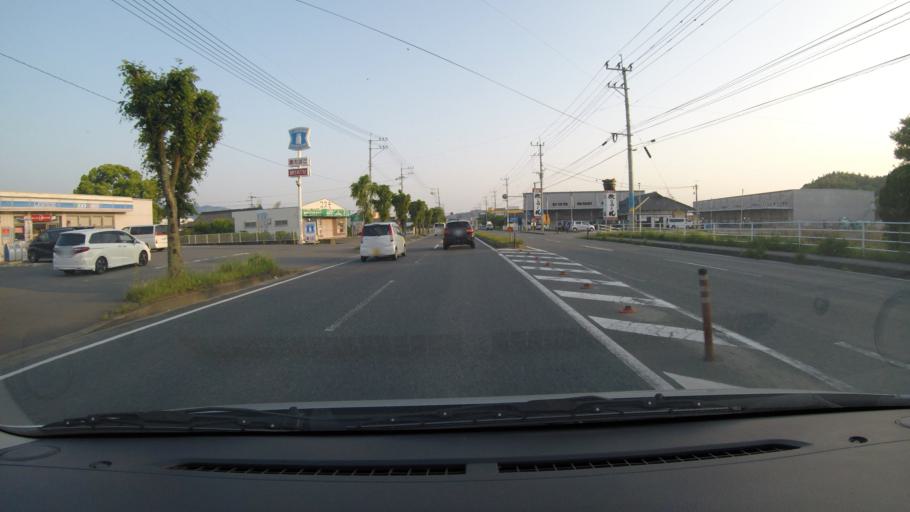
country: JP
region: Fukuoka
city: Sasaguri
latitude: 33.6442
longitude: 130.4962
